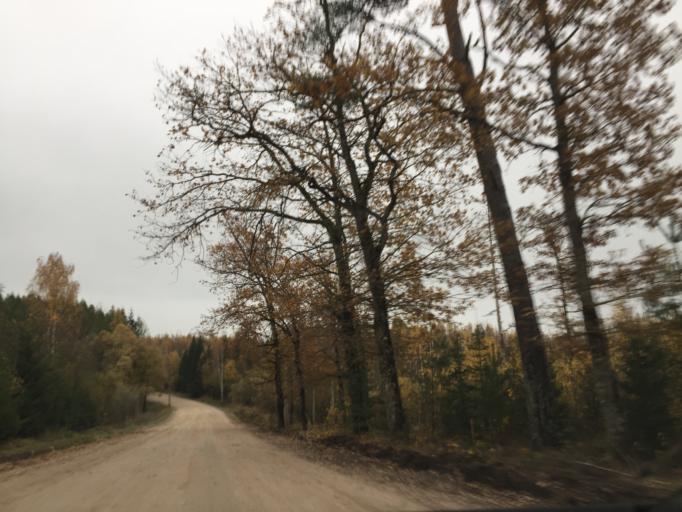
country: LV
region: Sigulda
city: Sigulda
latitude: 57.2740
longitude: 24.8262
